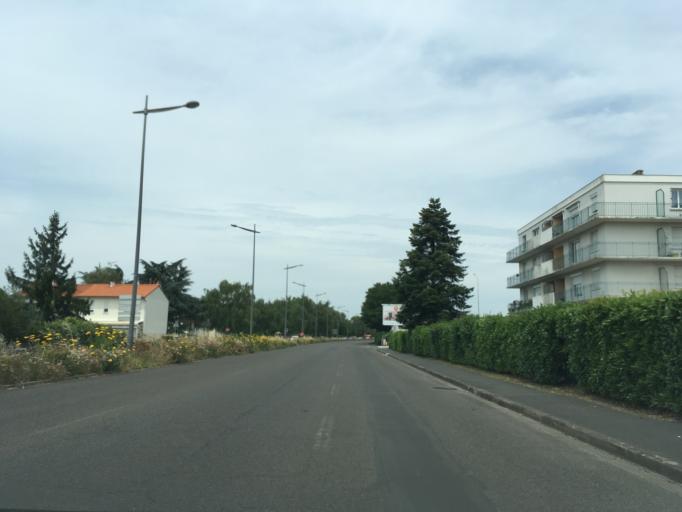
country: FR
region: Poitou-Charentes
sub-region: Departement des Deux-Sevres
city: Niort
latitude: 46.3200
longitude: -0.4860
